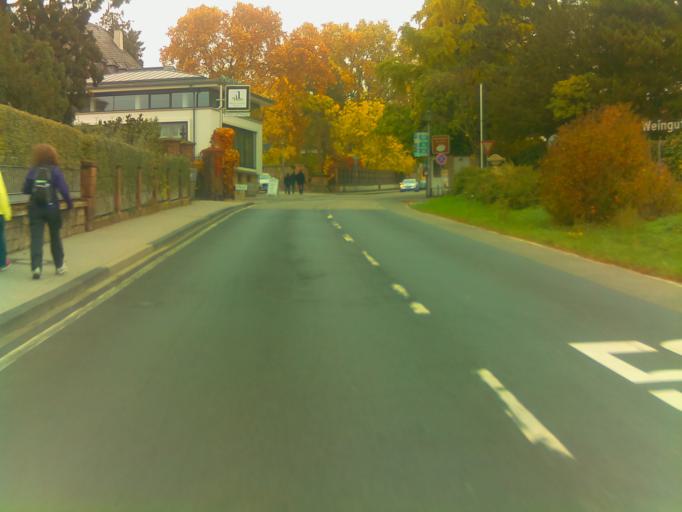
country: DE
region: Rheinland-Pfalz
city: Wachenheim
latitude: 49.4360
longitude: 8.1840
